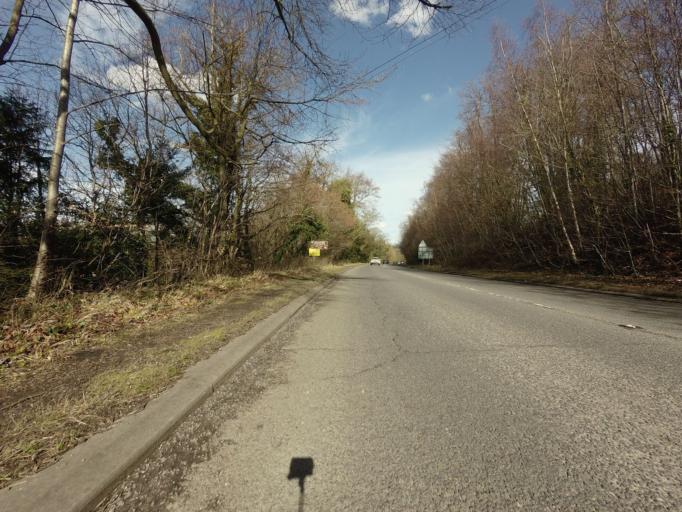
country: GB
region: England
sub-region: Kent
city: Eynsford
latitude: 51.3578
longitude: 0.2010
